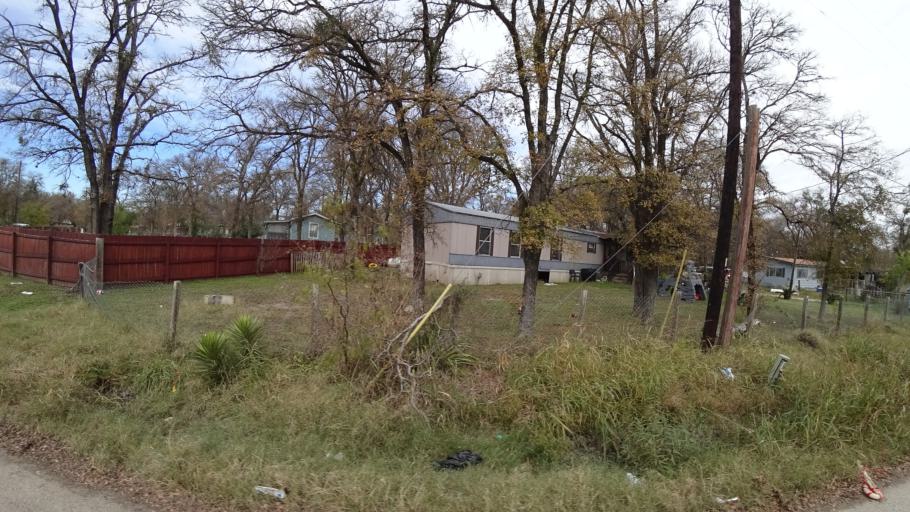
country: US
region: Texas
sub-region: Travis County
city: Garfield
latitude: 30.1320
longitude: -97.5666
